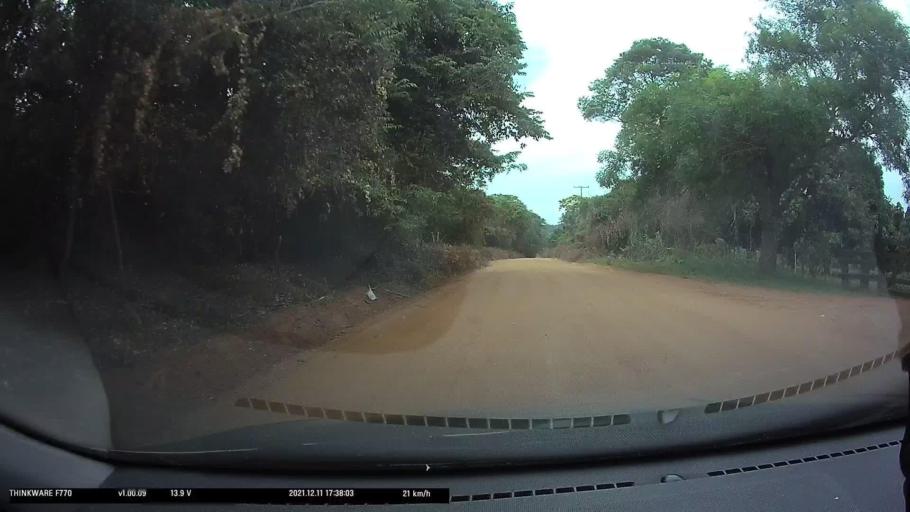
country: PY
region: Cordillera
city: Altos
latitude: -25.3017
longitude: -57.2579
